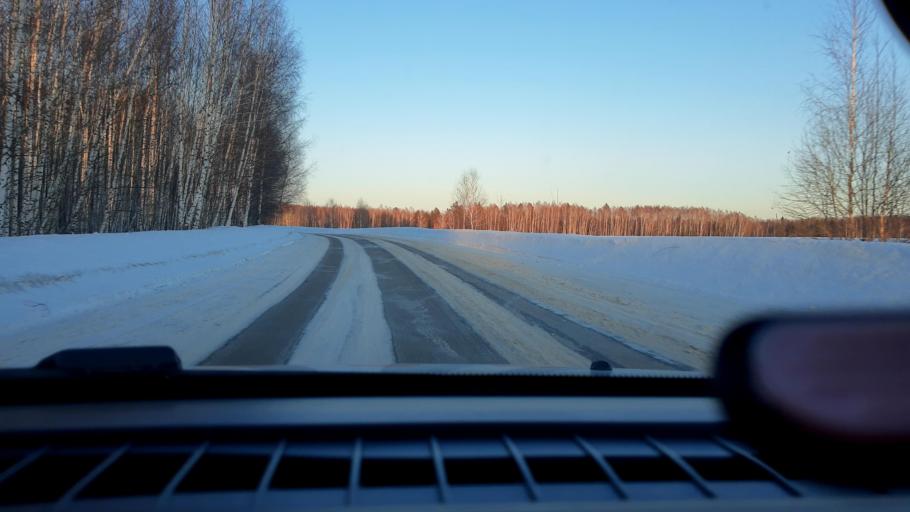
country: RU
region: Nizjnij Novgorod
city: Pervoye Maya
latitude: 56.1581
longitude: 44.8973
